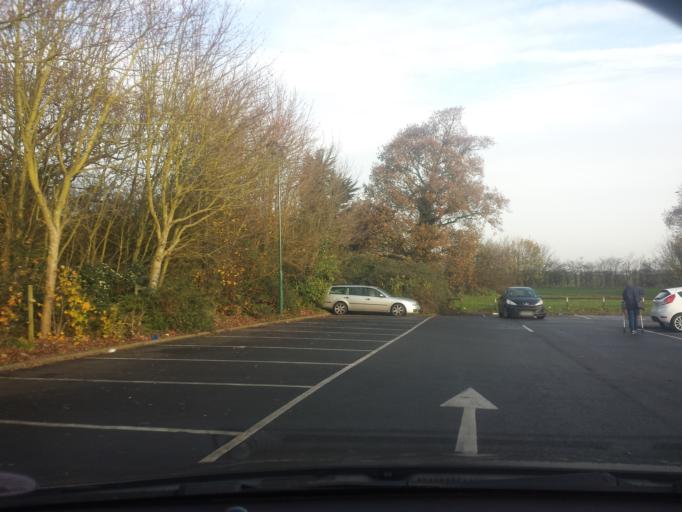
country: GB
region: England
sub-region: Essex
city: Little Clacton
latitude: 51.8195
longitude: 1.1488
